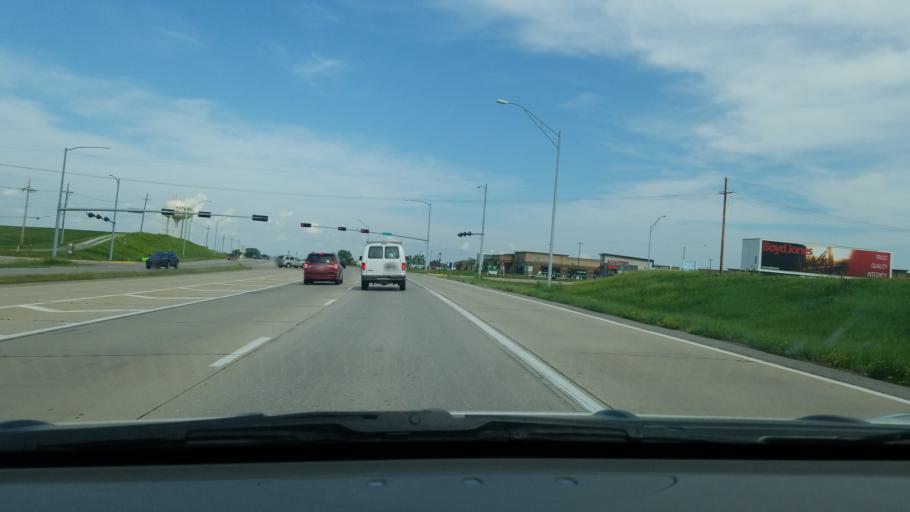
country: US
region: Nebraska
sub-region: Sarpy County
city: Papillion
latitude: 41.1398
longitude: -96.0547
